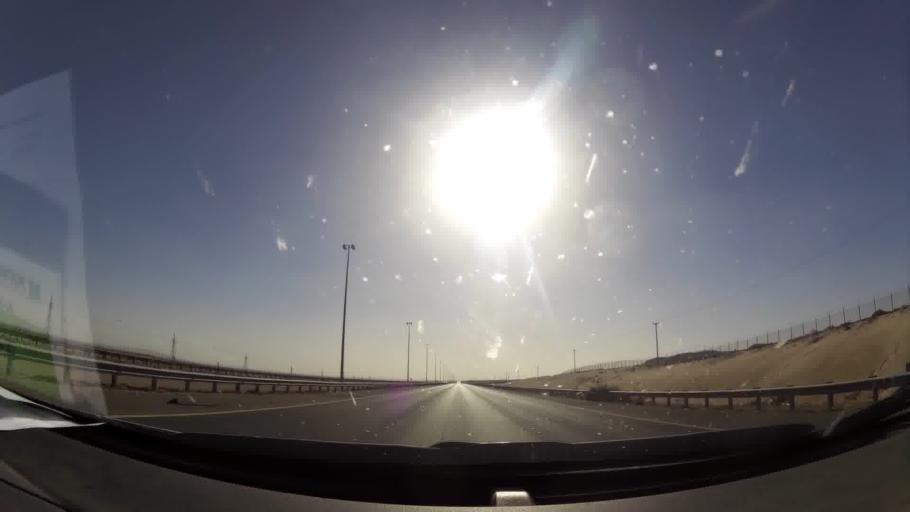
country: KW
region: Muhafazat al Jahra'
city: Al Jahra'
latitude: 29.5114
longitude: 47.8020
